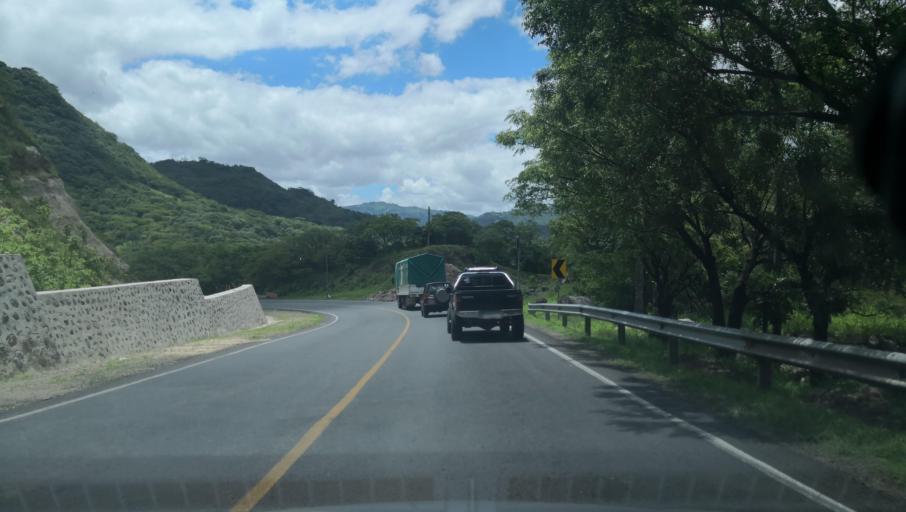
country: NI
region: Esteli
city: Condega
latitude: 13.2671
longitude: -86.3550
